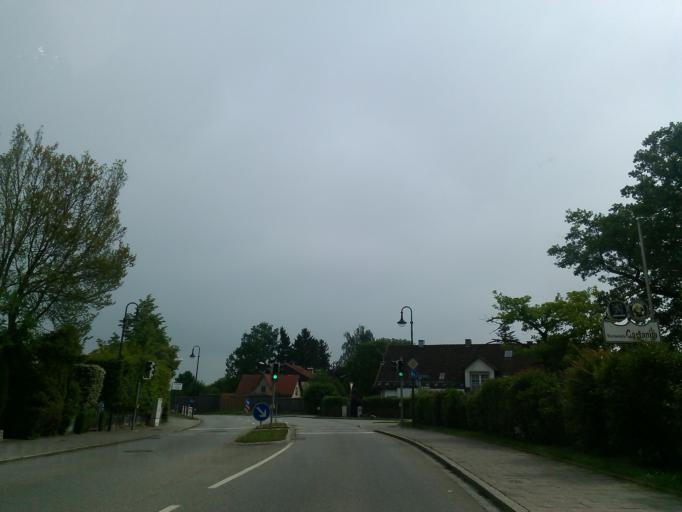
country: DE
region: Bavaria
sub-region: Upper Bavaria
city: Eichenau
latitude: 48.1766
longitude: 11.3302
